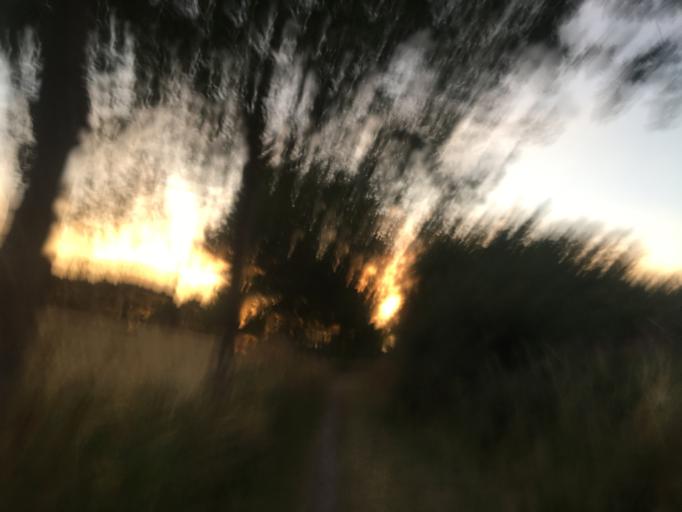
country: DK
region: Central Jutland
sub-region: Syddjurs Kommune
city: Hornslet
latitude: 56.3216
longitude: 10.3340
